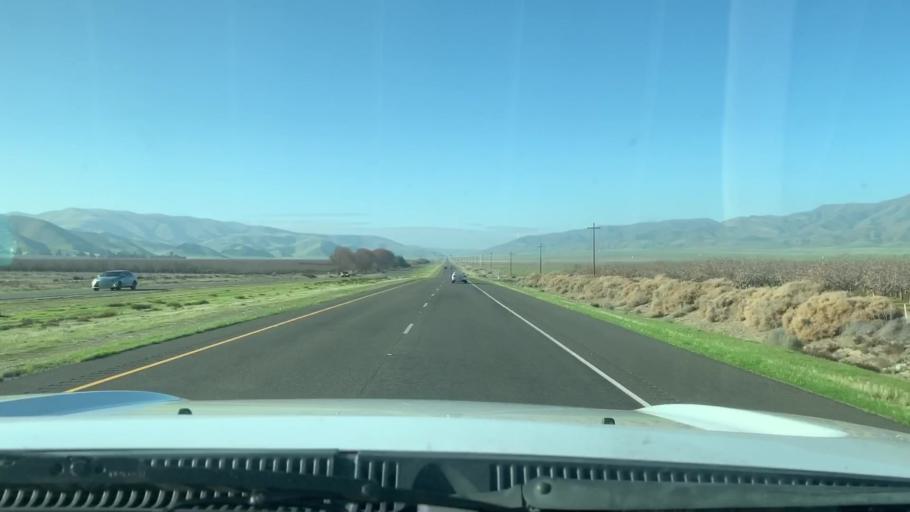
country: US
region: California
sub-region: San Luis Obispo County
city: Shandon
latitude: 35.6760
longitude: -120.0921
